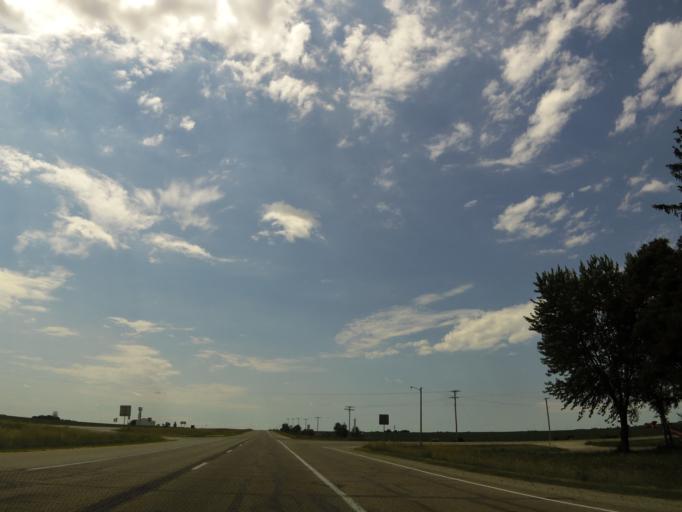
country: US
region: Iowa
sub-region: Bremer County
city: Tripoli
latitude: 42.7746
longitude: -92.3374
